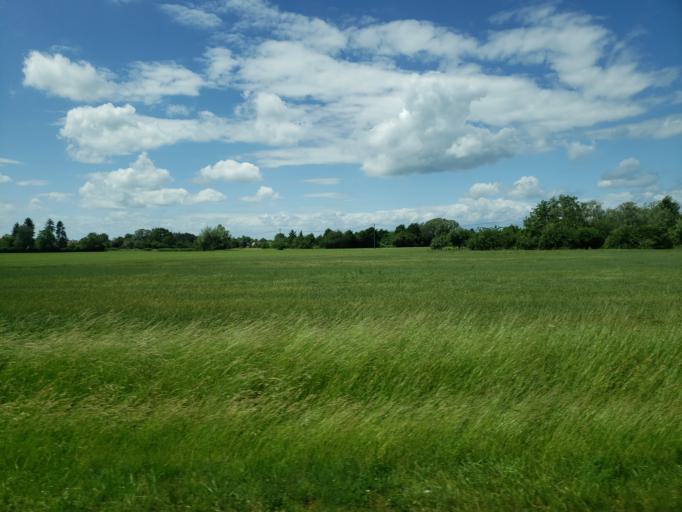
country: FR
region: Bourgogne
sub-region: Departement de l'Yonne
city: Migennes
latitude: 47.9507
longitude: 3.5039
